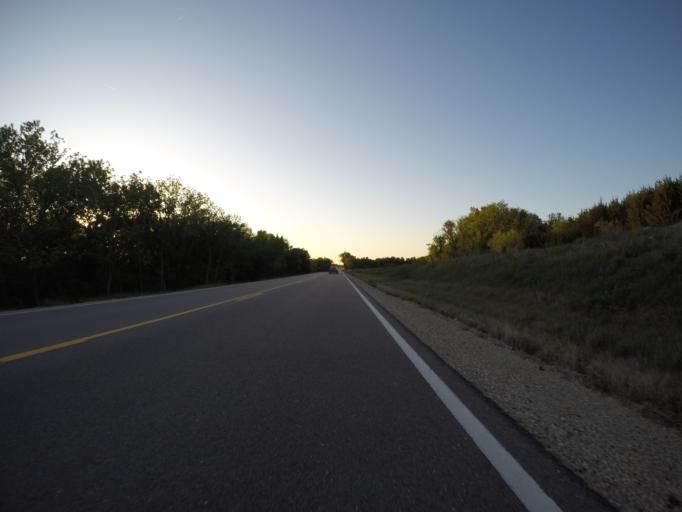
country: US
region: Kansas
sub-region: Riley County
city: Fort Riley North
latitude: 39.2535
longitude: -96.7722
